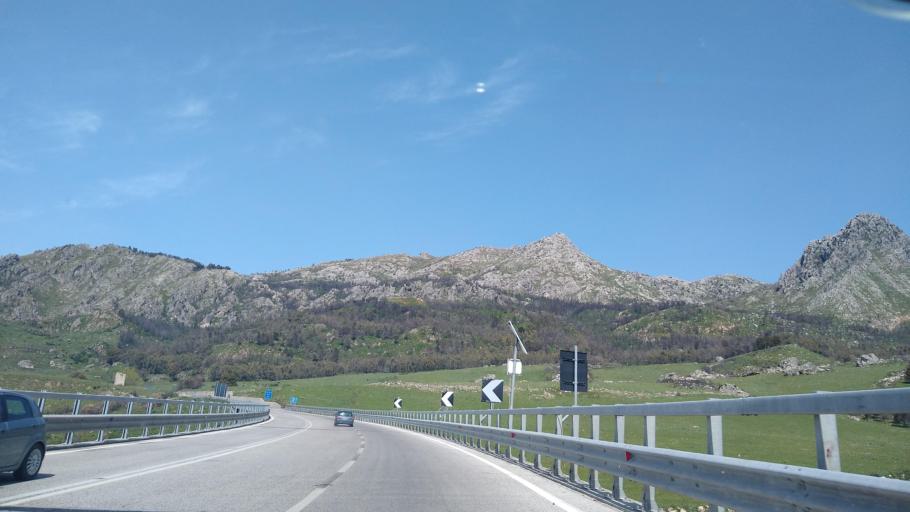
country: IT
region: Sicily
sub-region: Palermo
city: San Giuseppe Jato
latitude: 37.9828
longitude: 13.2367
